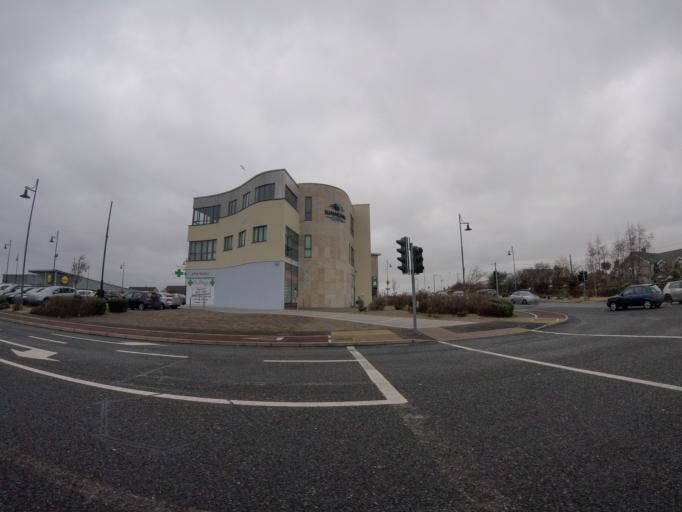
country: IE
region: Munster
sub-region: Waterford
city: Tra Mhor
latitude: 52.1643
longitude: -7.1608
